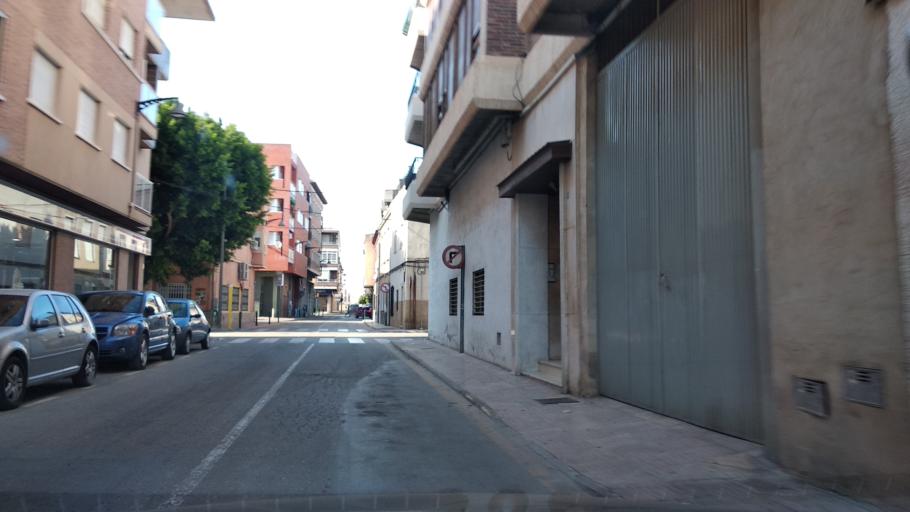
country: ES
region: Murcia
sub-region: Murcia
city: Santomera
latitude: 38.0590
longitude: -1.0477
